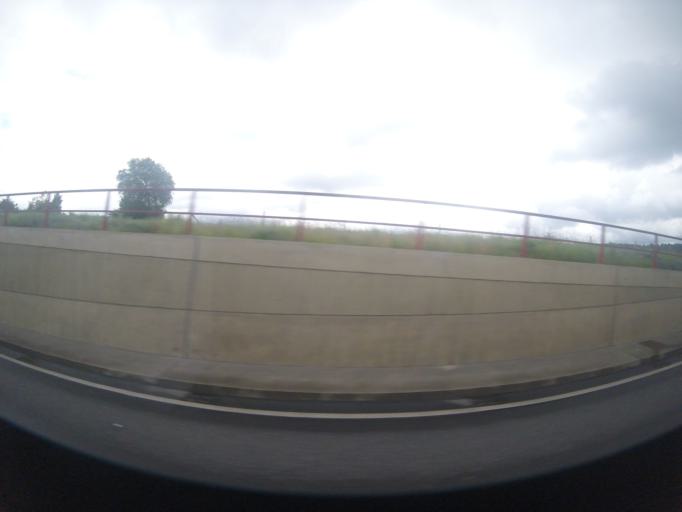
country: DE
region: Saarland
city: Uberherrn
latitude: 49.2462
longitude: 6.7169
